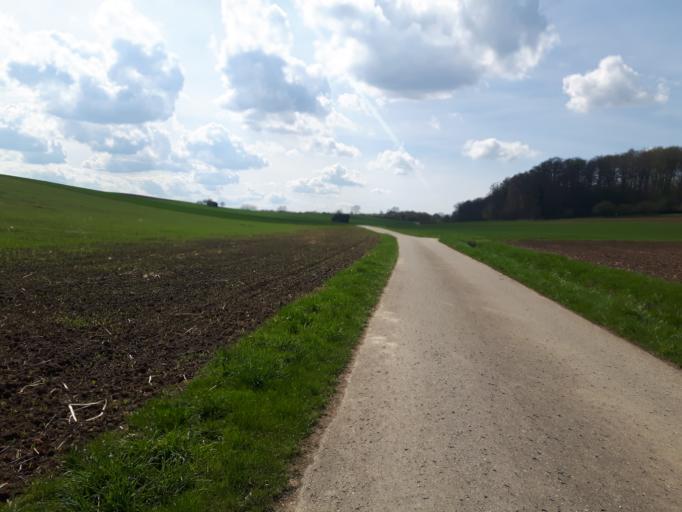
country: DE
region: Baden-Wuerttemberg
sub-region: Regierungsbezirk Stuttgart
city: Gemmingen
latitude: 49.1405
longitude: 9.0162
